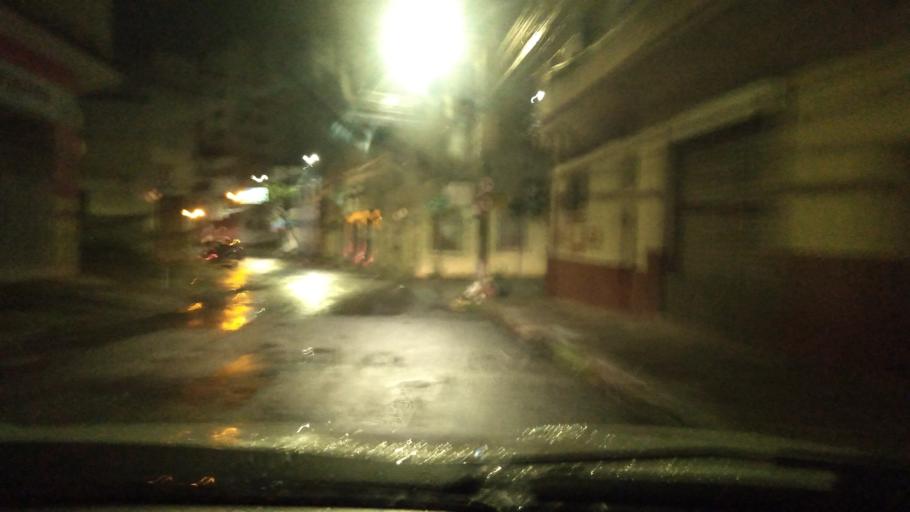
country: BR
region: Minas Gerais
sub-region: Belo Horizonte
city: Belo Horizonte
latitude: -19.9122
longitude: -43.9485
